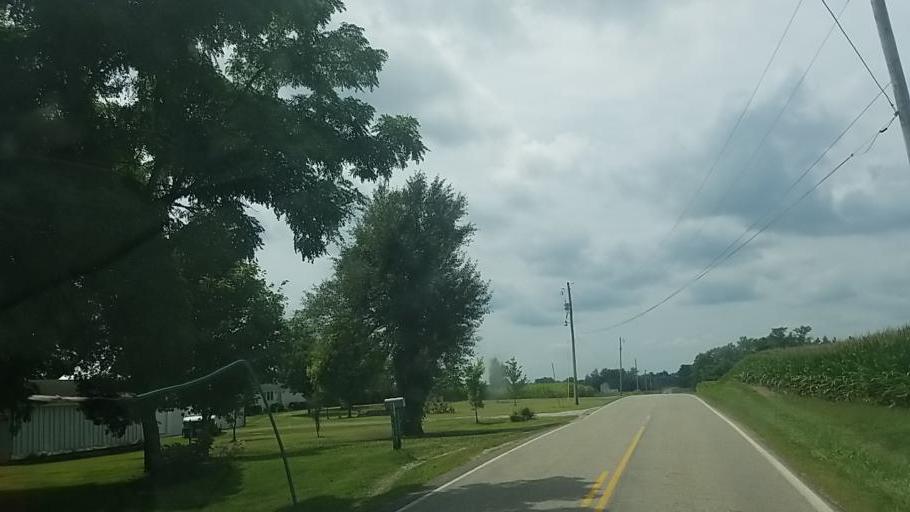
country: US
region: Ohio
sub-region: Fairfield County
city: Lithopolis
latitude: 39.7516
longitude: -82.8308
